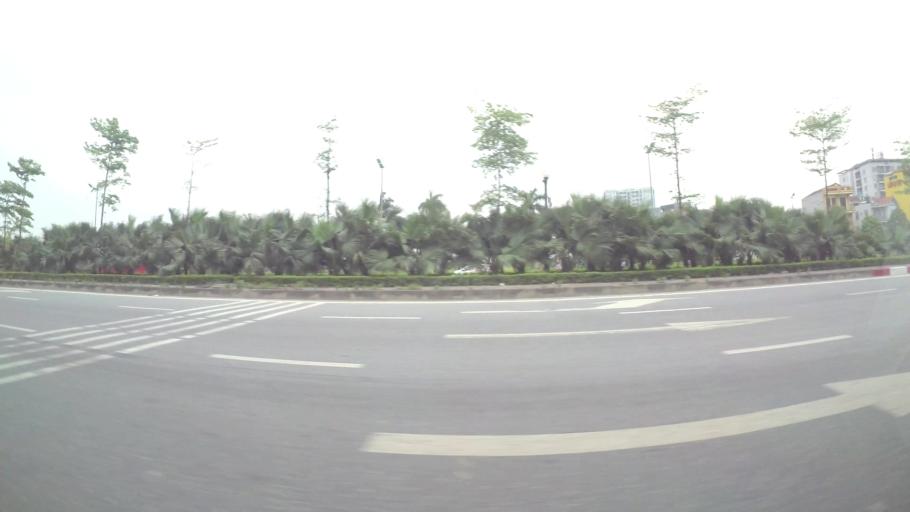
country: VN
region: Ha Noi
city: Hoan Kiem
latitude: 21.0626
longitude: 105.8822
